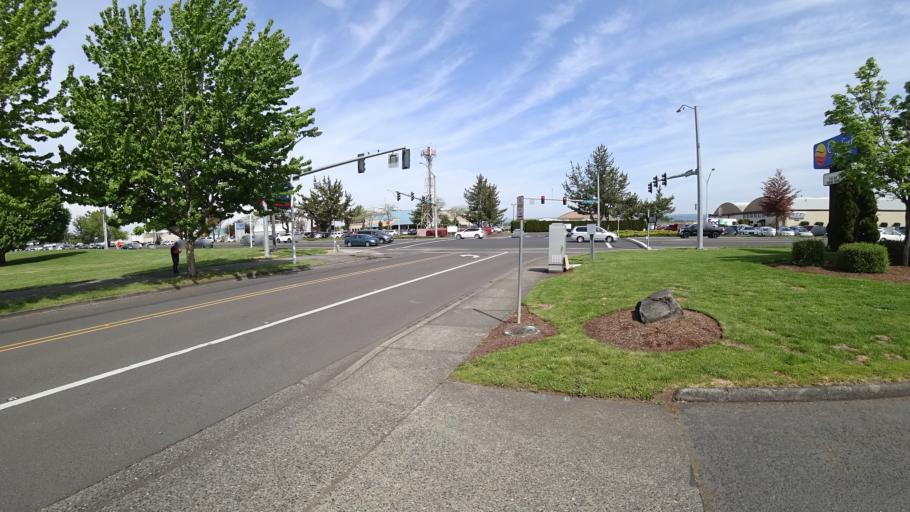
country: US
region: Oregon
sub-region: Washington County
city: Hillsboro
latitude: 45.5318
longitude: -122.9466
